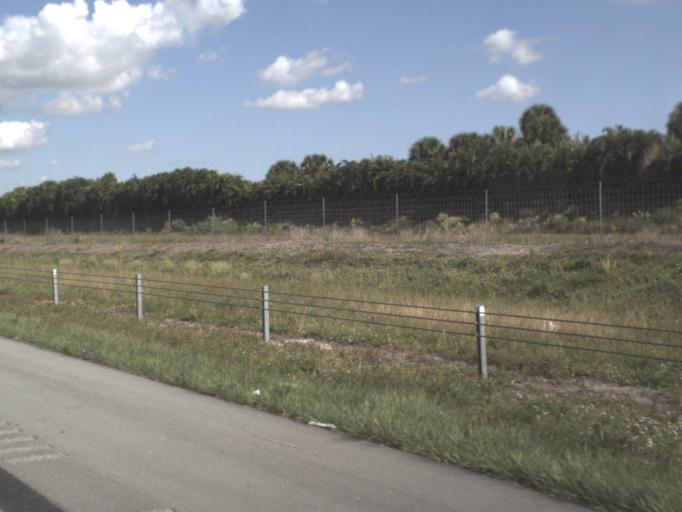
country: US
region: Florida
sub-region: Palm Beach County
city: Boca Del Mar
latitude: 26.3899
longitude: -80.1710
